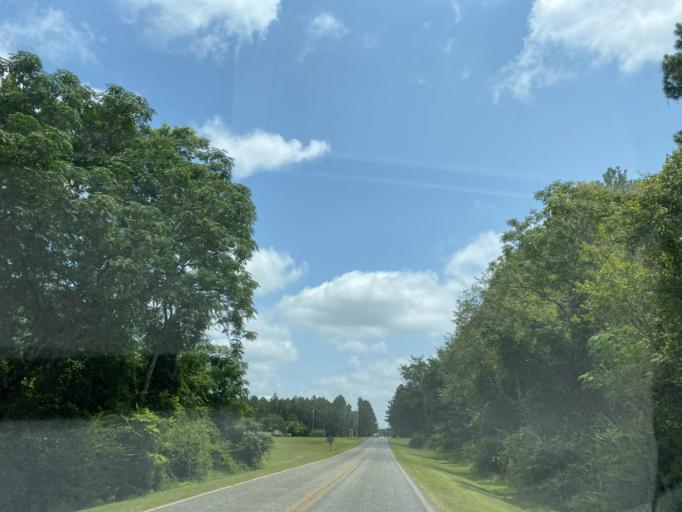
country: US
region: Georgia
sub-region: Wheeler County
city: Alamo
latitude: 32.1028
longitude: -82.7691
